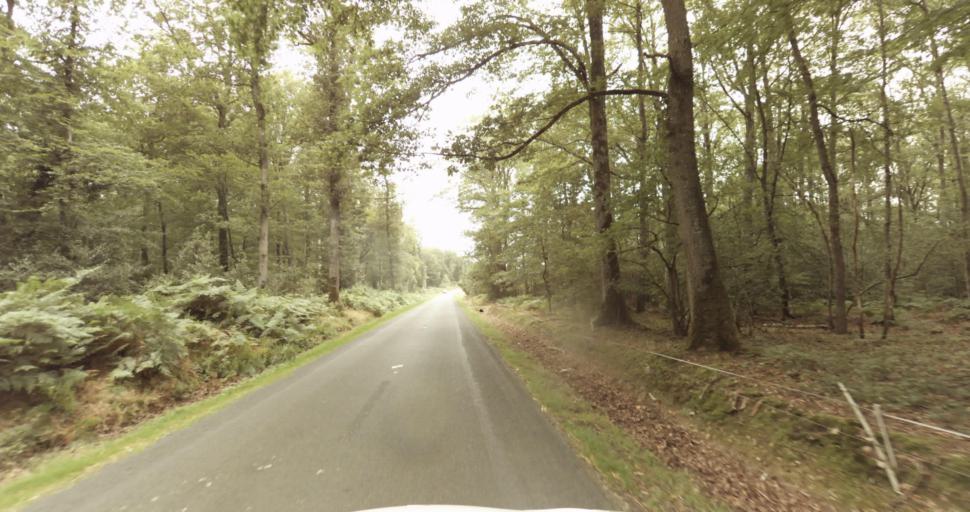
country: FR
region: Haute-Normandie
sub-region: Departement de l'Eure
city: Arnieres-sur-Iton
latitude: 48.9503
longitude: 1.0700
